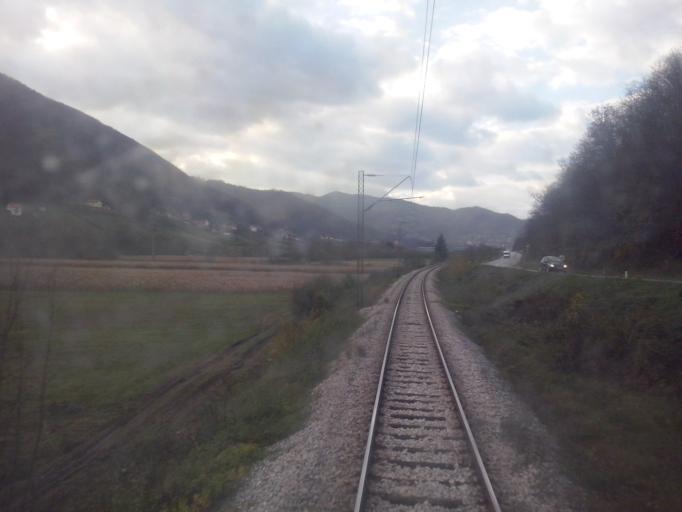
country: RS
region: Central Serbia
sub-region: Zlatiborski Okrug
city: Kosjeric
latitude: 43.9847
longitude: 19.9336
